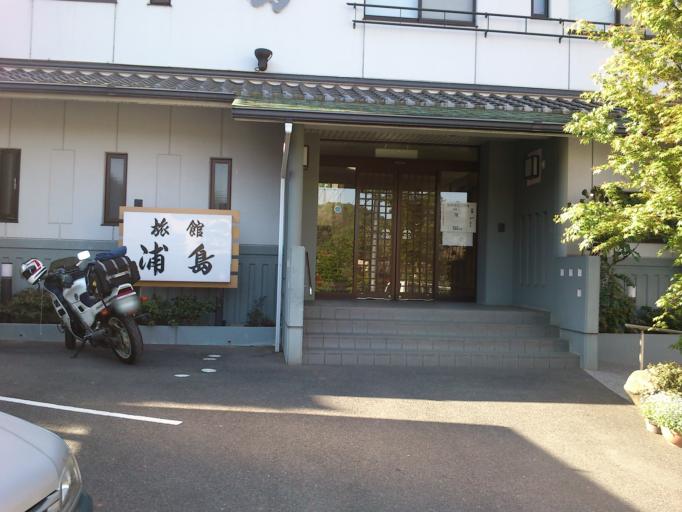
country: JP
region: Hiroshima
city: Onomichi
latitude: 34.4486
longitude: 133.1989
